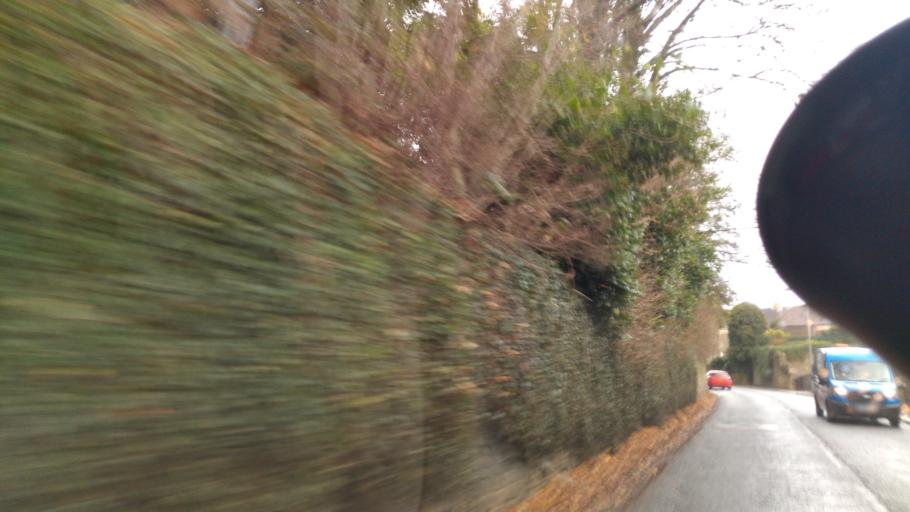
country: GB
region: England
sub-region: Wiltshire
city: Bradford-on-Avon
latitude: 51.3495
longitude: -2.2505
